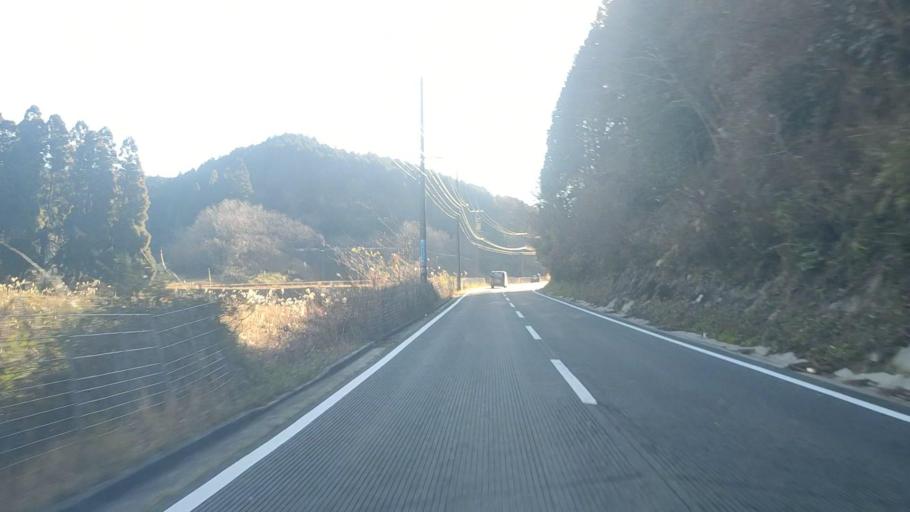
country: JP
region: Saga Prefecture
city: Kanzakimachi-kanzaki
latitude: 33.4163
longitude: 130.2784
